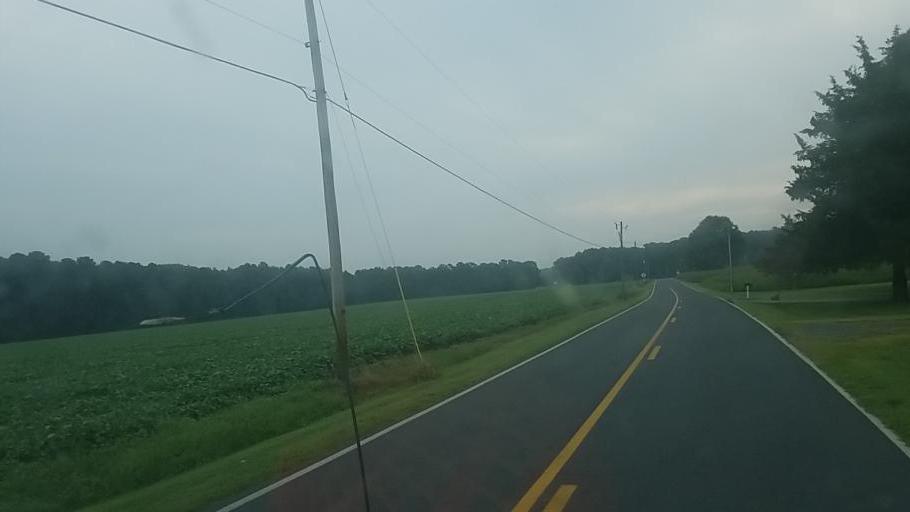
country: US
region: Maryland
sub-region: Wicomico County
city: Delmar
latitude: 38.4006
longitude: -75.5322
